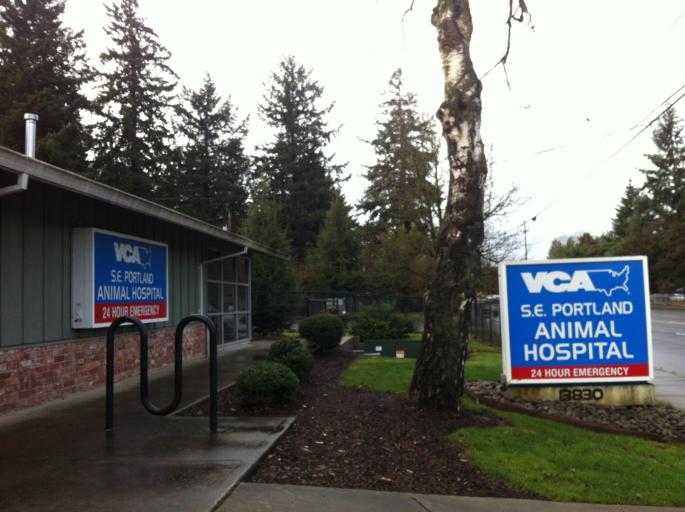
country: US
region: Oregon
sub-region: Multnomah County
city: Lents
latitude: 45.5189
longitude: -122.5215
